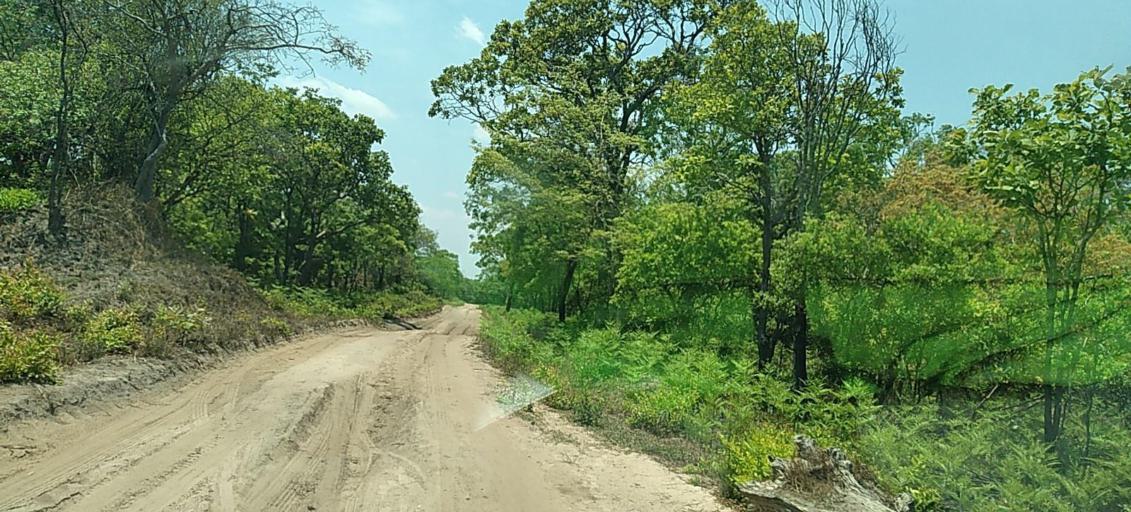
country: CD
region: Katanga
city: Kolwezi
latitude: -11.3455
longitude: 25.2163
